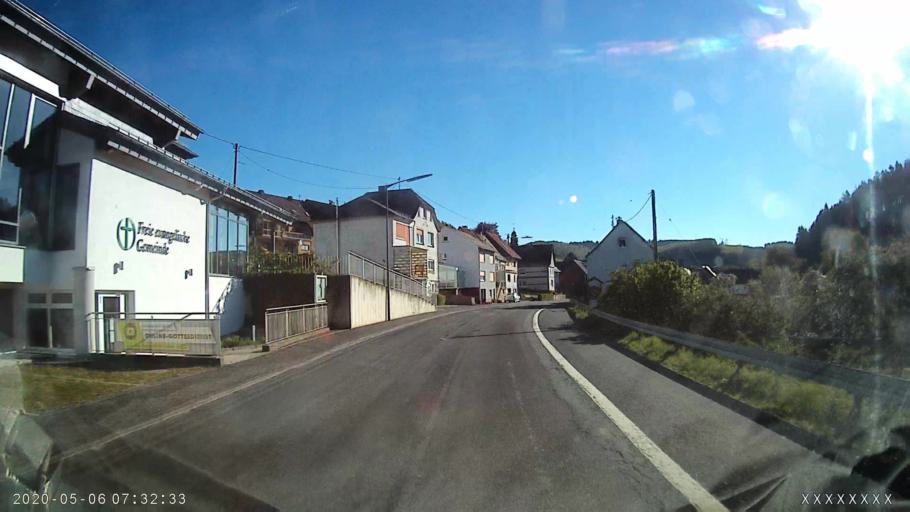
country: DE
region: Hesse
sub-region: Regierungsbezirk Giessen
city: Haiger
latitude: 50.8247
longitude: 8.2274
